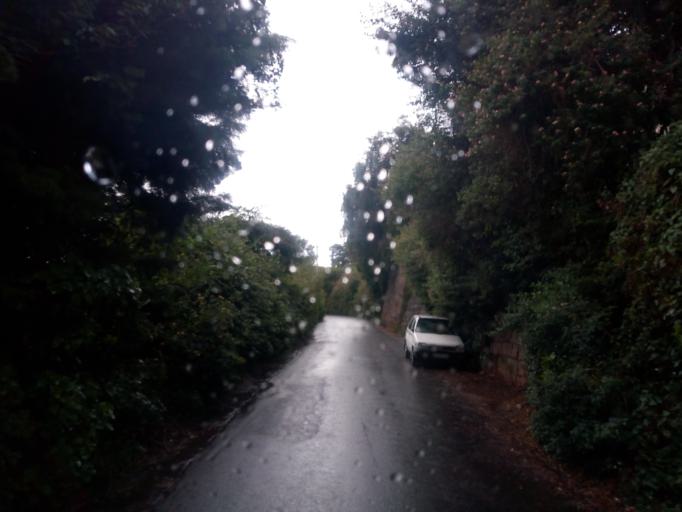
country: IN
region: Tamil Nadu
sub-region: Nilgiri
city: Wellington
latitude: 11.3479
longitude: 76.8017
